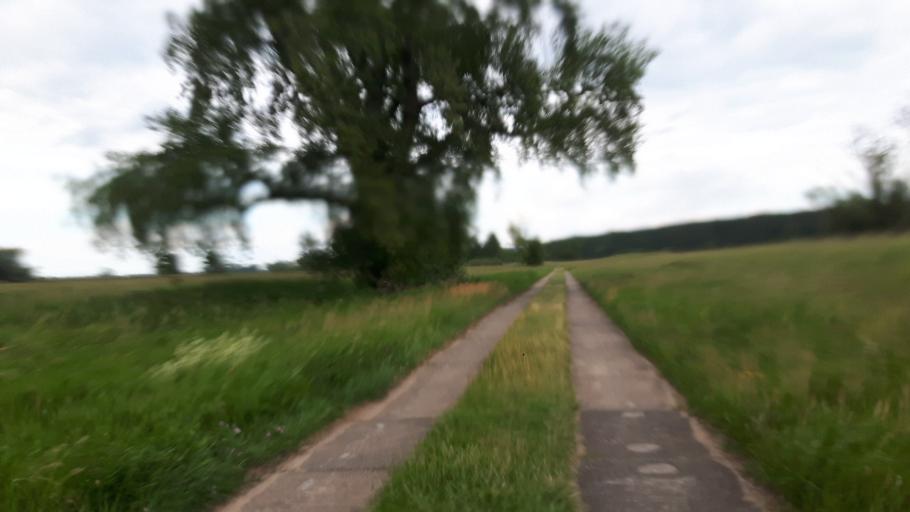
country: PL
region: West Pomeranian Voivodeship
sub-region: Powiat gryfinski
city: Widuchowa
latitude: 53.1075
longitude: 14.3718
